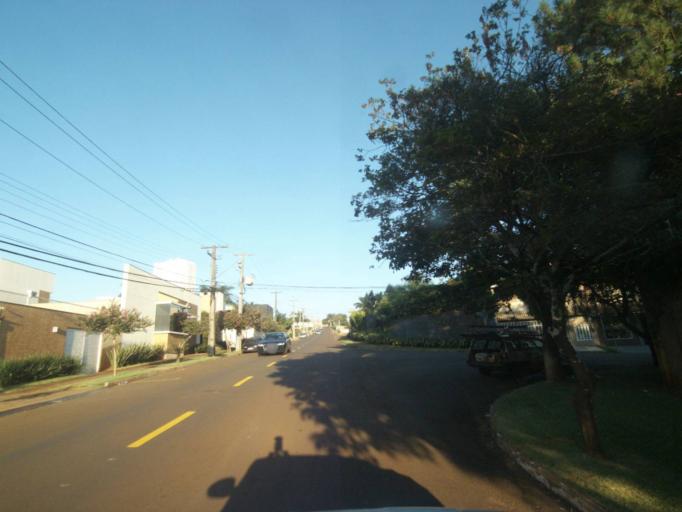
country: BR
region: Parana
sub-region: Londrina
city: Londrina
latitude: -23.3459
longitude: -51.1936
